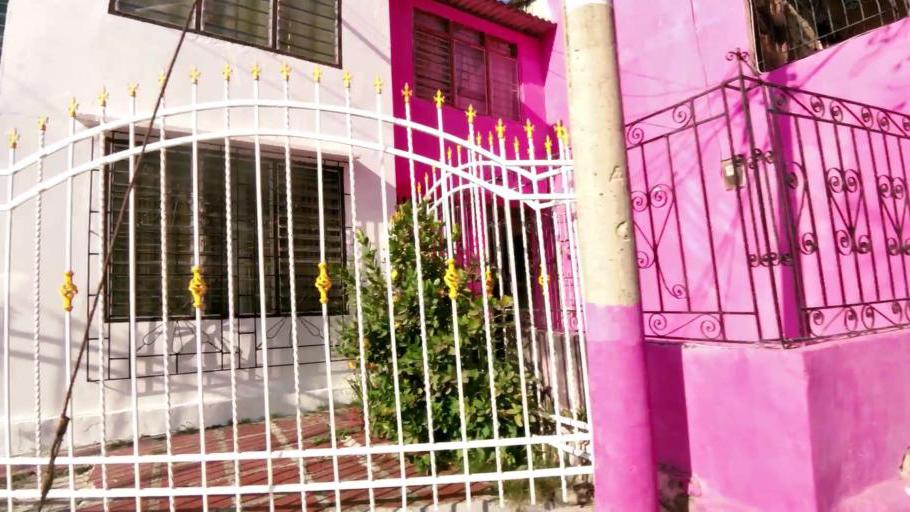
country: CO
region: Bolivar
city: Cartagena
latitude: 10.3842
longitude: -75.4817
